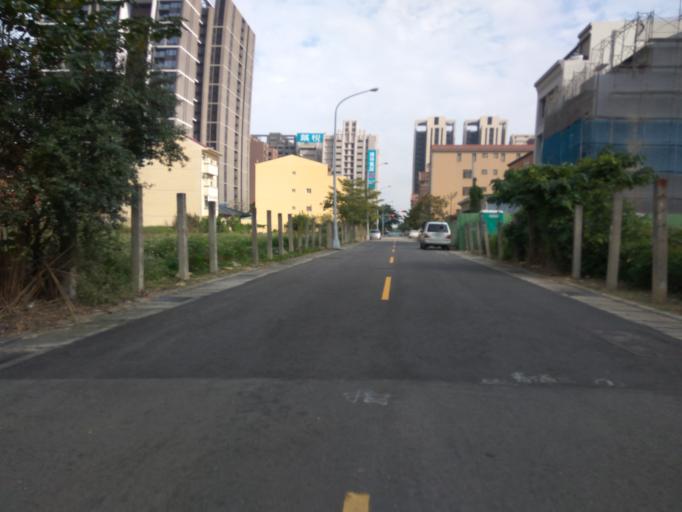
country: TW
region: Taiwan
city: Taoyuan City
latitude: 25.0063
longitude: 121.2192
